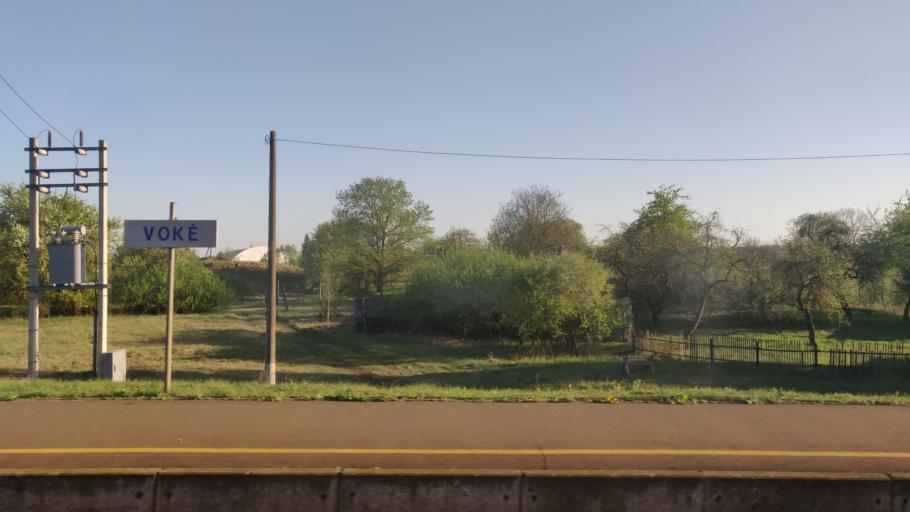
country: LT
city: Grigiskes
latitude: 54.6334
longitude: 25.1281
